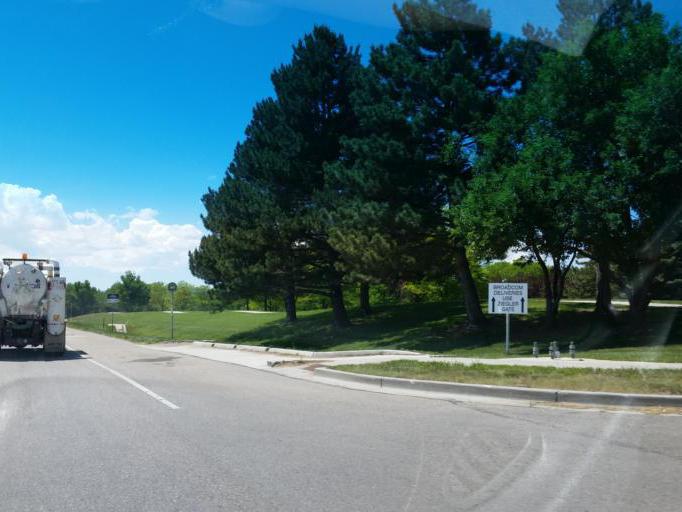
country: US
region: Colorado
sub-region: Larimer County
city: Fort Collins
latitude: 40.5235
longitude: -105.0156
